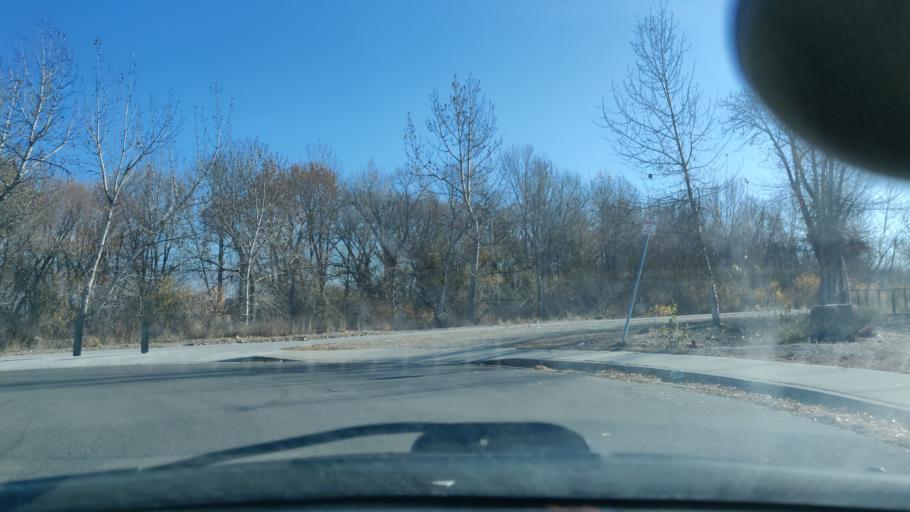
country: US
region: Idaho
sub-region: Ada County
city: Garden City
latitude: 43.6383
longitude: -116.2452
